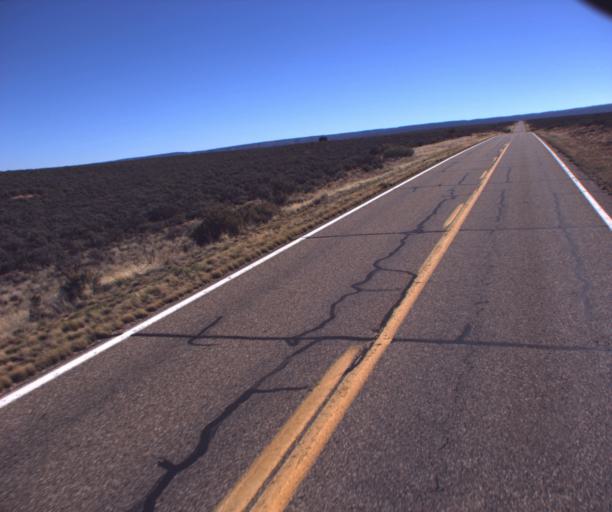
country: US
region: Arizona
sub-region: Coconino County
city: Fredonia
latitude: 36.9030
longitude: -112.3822
